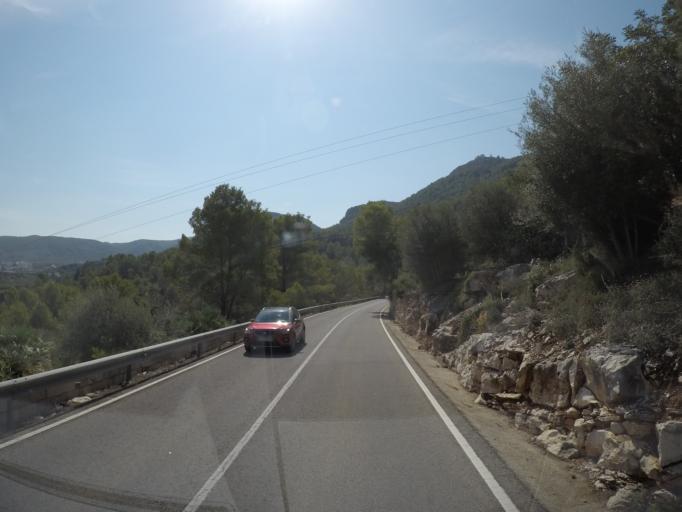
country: ES
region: Valencia
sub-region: Provincia de Alicante
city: Orba
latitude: 38.7817
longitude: -0.0794
